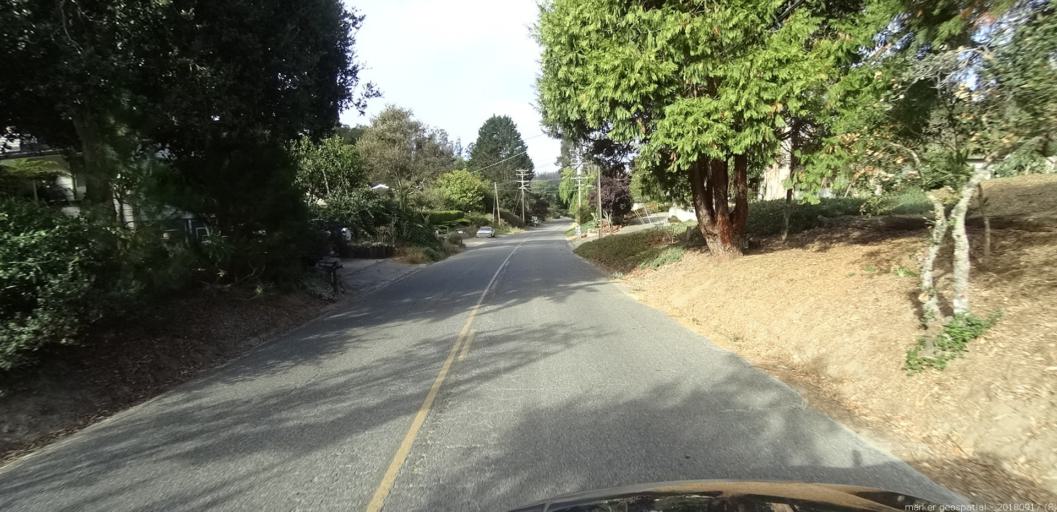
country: US
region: California
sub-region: Monterey County
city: Elkhorn
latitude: 36.8161
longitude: -121.6950
